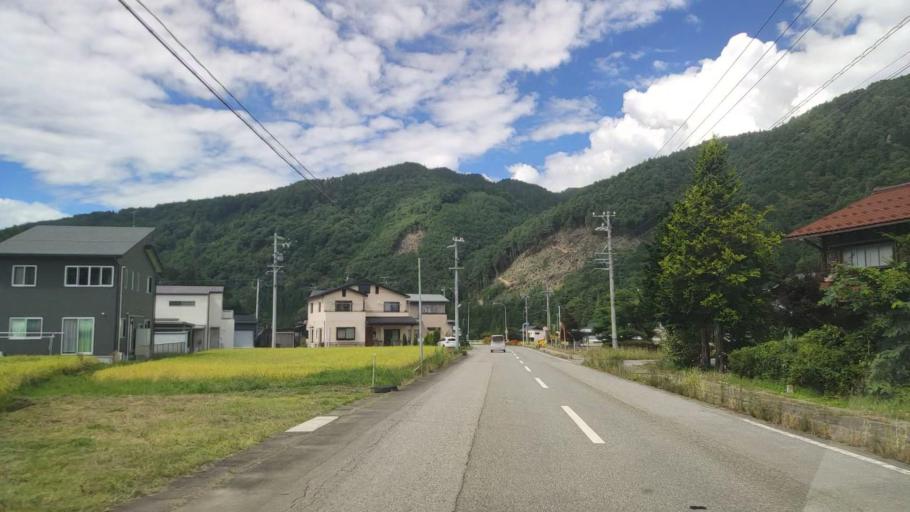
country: JP
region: Gifu
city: Takayama
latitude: 36.1783
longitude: 137.2829
